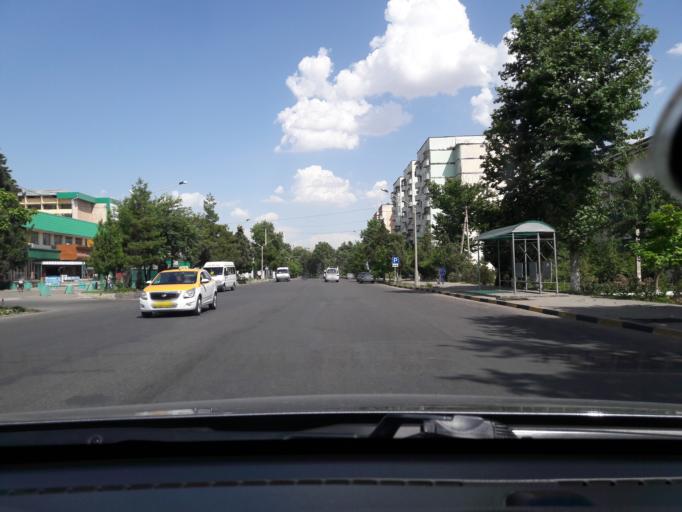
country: TJ
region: Dushanbe
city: Dushanbe
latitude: 38.5189
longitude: 68.7492
